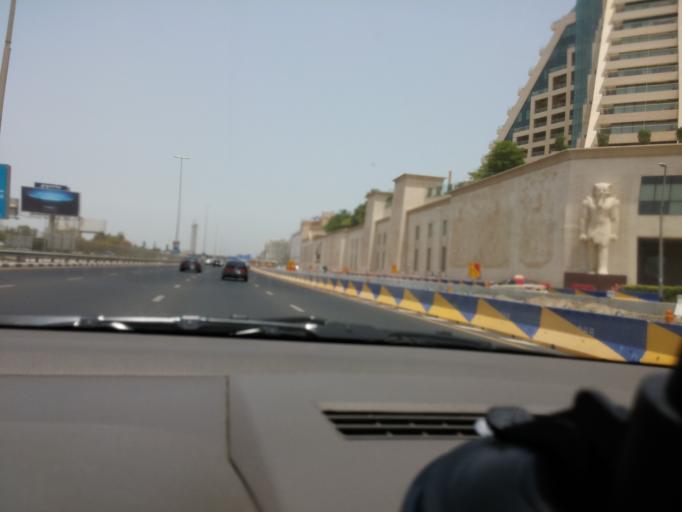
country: AE
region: Ash Shariqah
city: Sharjah
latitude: 25.2265
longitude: 55.3211
